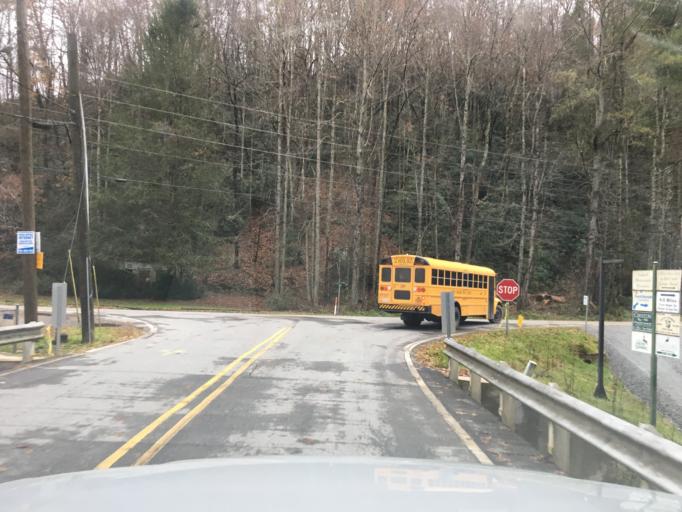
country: US
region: North Carolina
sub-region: Rutherford County
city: Lake Lure
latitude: 35.5236
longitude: -82.2488
